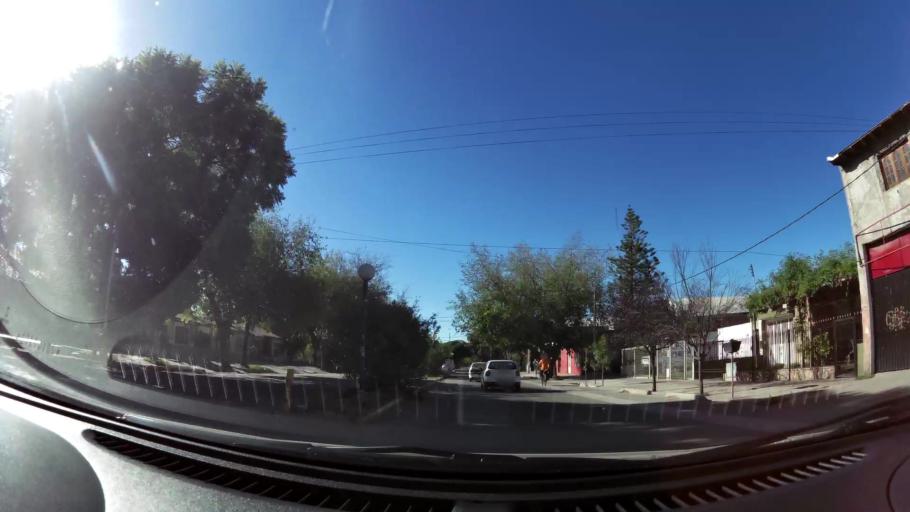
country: AR
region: Mendoza
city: Las Heras
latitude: -32.8588
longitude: -68.8213
